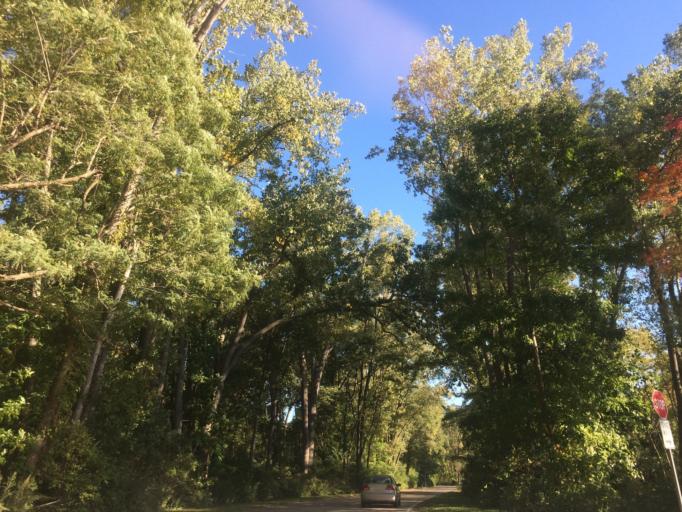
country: US
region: Pennsylvania
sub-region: Erie County
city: Erie
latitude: 42.1252
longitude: -80.1469
